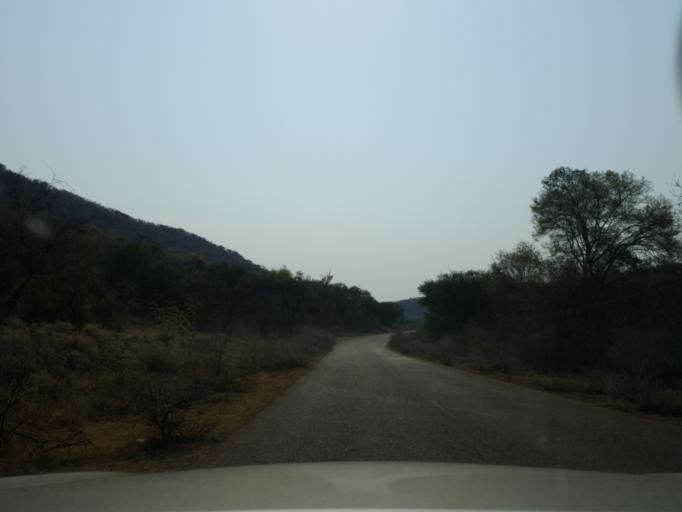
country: BW
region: South East
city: Lobatse
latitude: -25.3292
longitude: 25.7820
